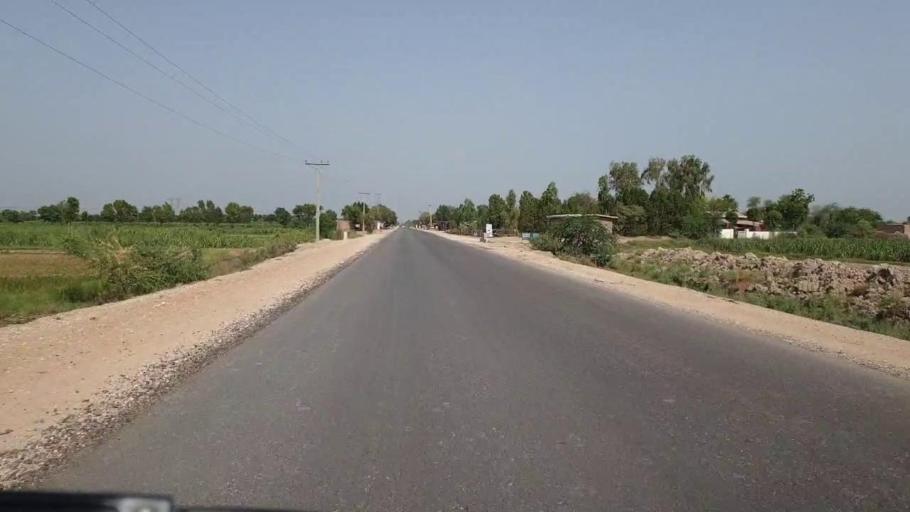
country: PK
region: Sindh
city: Sakrand
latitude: 26.2588
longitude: 68.1892
